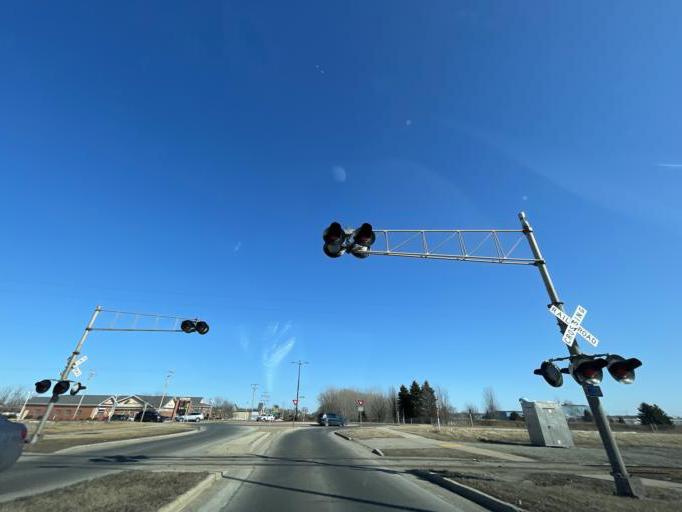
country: US
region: Wisconsin
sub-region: Brown County
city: Howard
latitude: 44.5909
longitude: -88.0787
